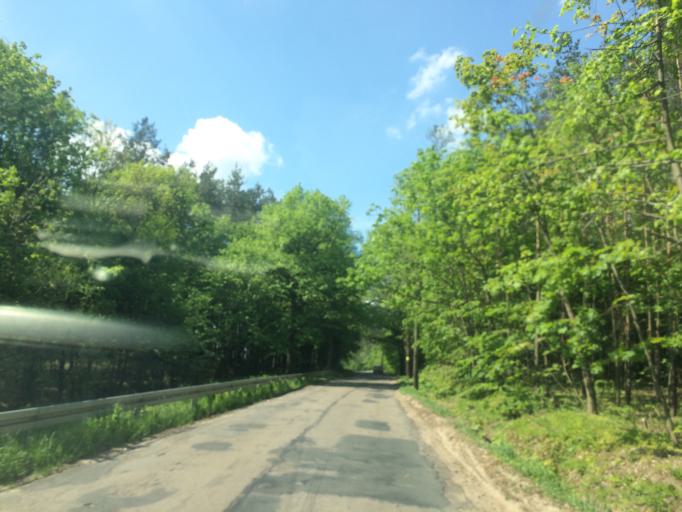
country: PL
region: Warmian-Masurian Voivodeship
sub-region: Powiat nowomiejski
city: Nowe Miasto Lubawskie
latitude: 53.4264
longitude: 19.6836
